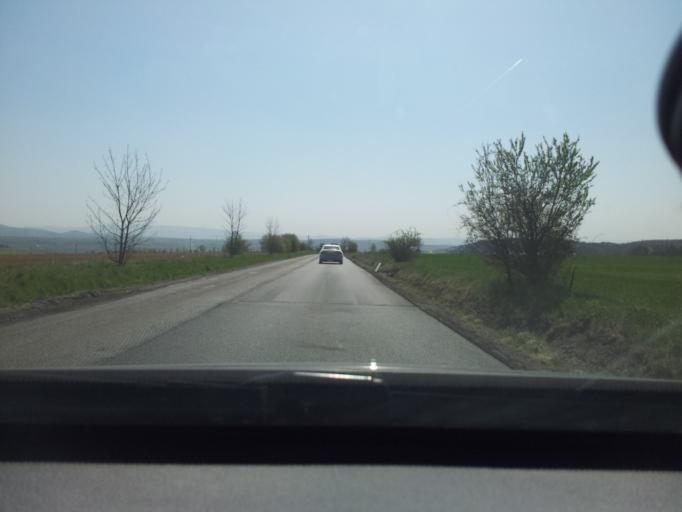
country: SK
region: Nitriansky
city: Banovce nad Bebravou
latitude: 48.7595
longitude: 18.1981
